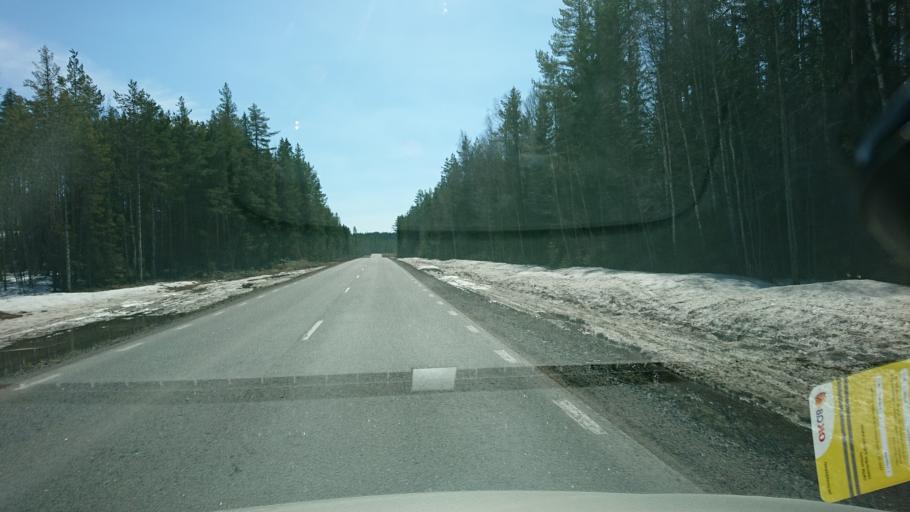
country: SE
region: Vaesternorrland
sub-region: Solleftea Kommun
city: As
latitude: 63.5908
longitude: 16.4324
